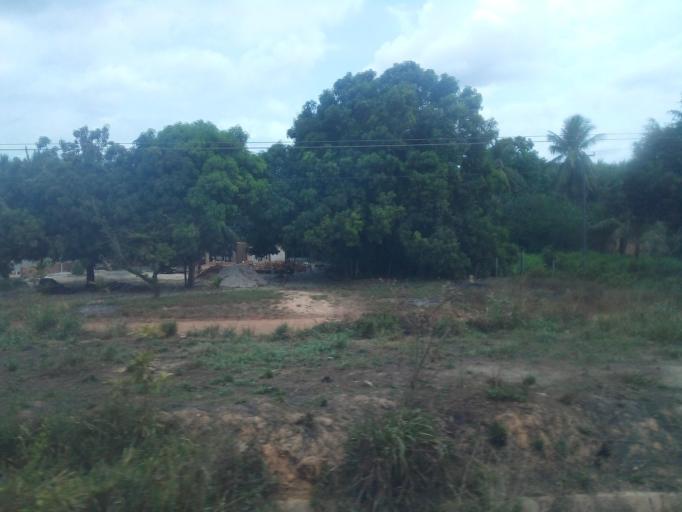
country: BR
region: Maranhao
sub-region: Santa Ines
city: Santa Ines
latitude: -3.7066
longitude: -46.0389
